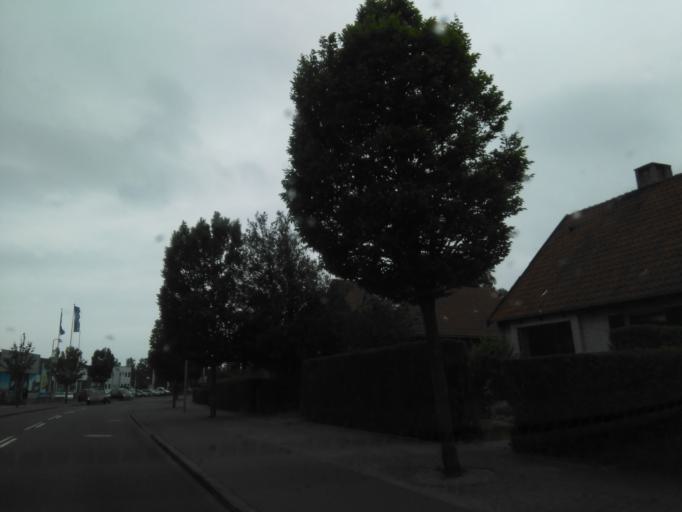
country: DK
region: Capital Region
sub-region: Bornholm Kommune
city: Ronne
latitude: 55.0969
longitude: 14.7119
